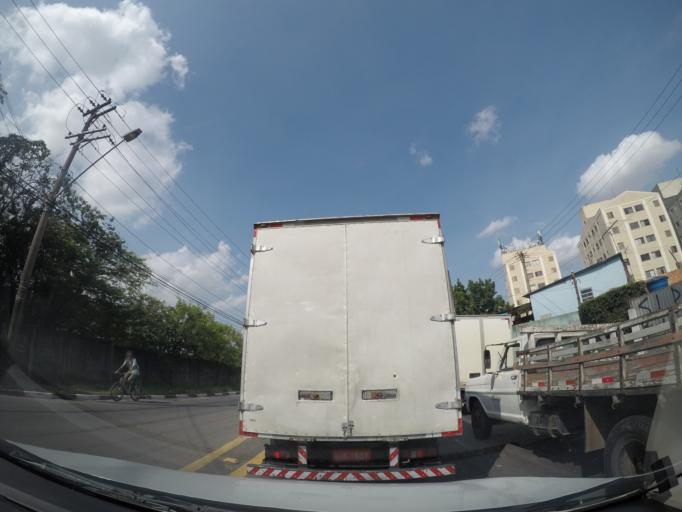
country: BR
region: Sao Paulo
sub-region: Guarulhos
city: Guarulhos
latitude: -23.4370
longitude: -46.4669
